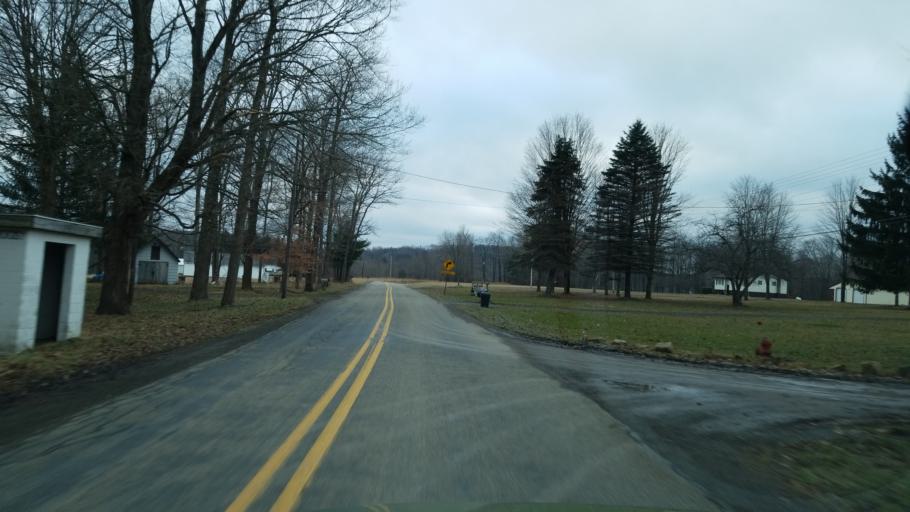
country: US
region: Pennsylvania
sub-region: Jefferson County
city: Falls Creek
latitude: 41.1606
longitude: -78.8182
